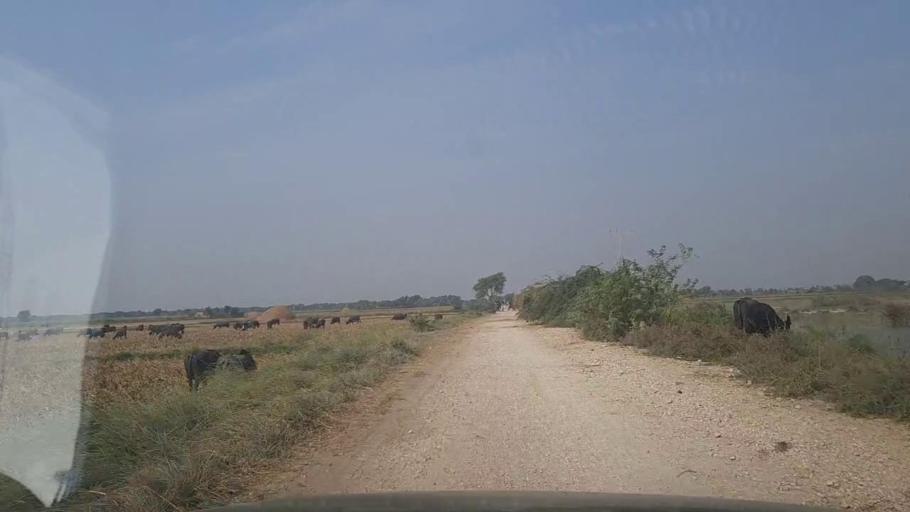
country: PK
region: Sindh
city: Bulri
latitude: 24.9741
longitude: 68.3053
